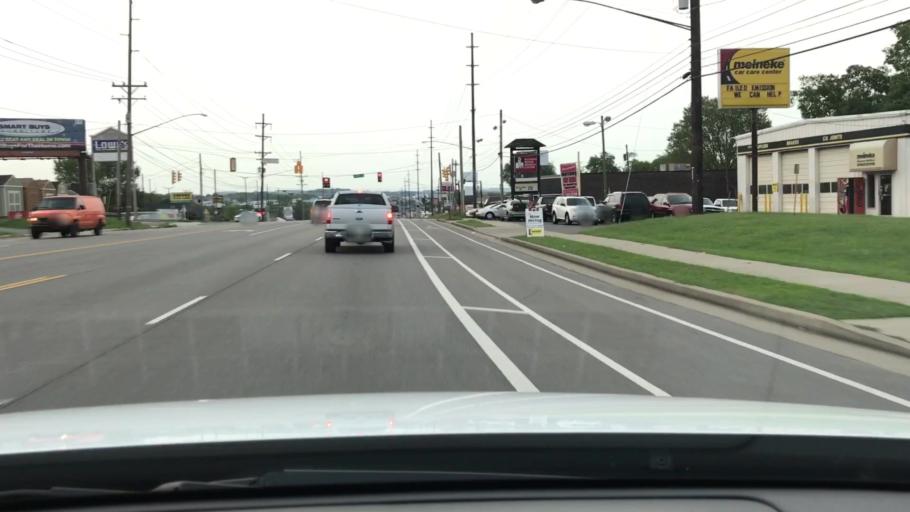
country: US
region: Tennessee
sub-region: Davidson County
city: Goodlettsville
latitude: 36.2785
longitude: -86.7091
